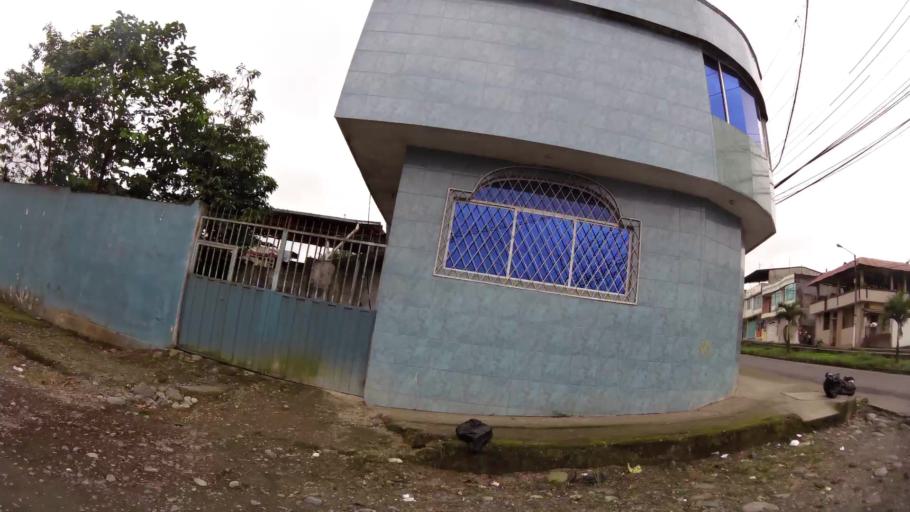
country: EC
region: Santo Domingo de los Tsachilas
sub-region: Canton Santo Domingo de los Colorados
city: Santo Domingo de los Colorados
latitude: -0.2488
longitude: -79.1978
